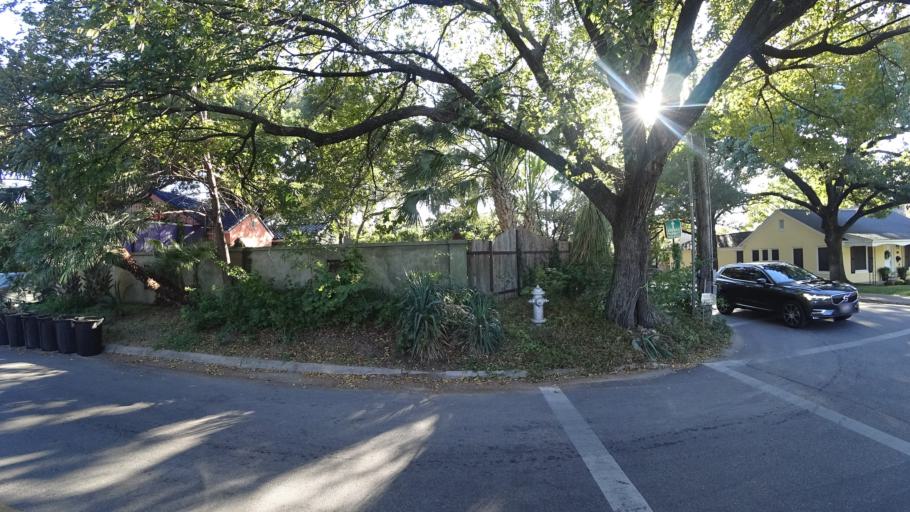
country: US
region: Texas
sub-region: Travis County
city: Austin
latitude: 30.3018
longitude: -97.7550
